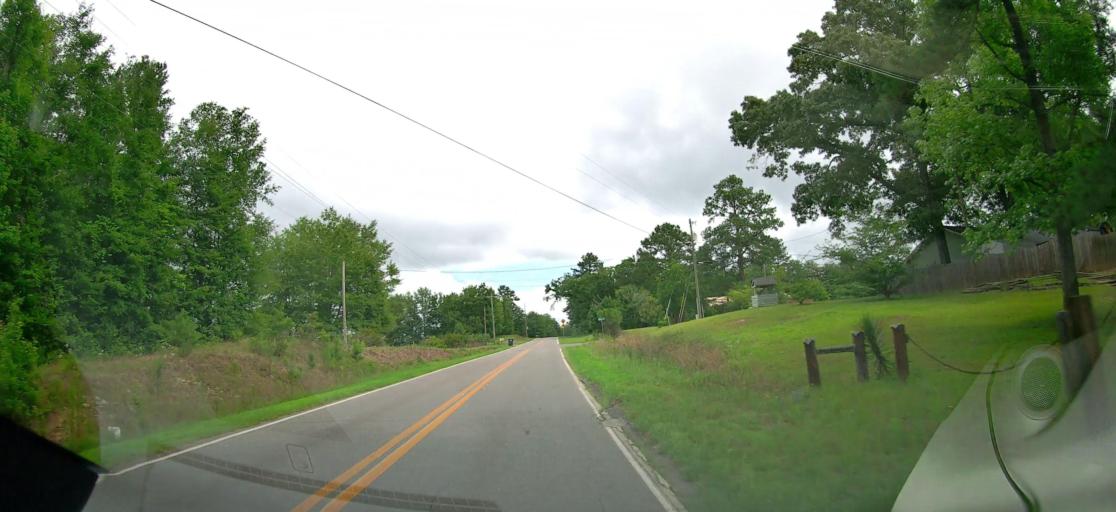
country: US
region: Georgia
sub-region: Bibb County
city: West Point
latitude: 32.7428
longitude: -83.7656
